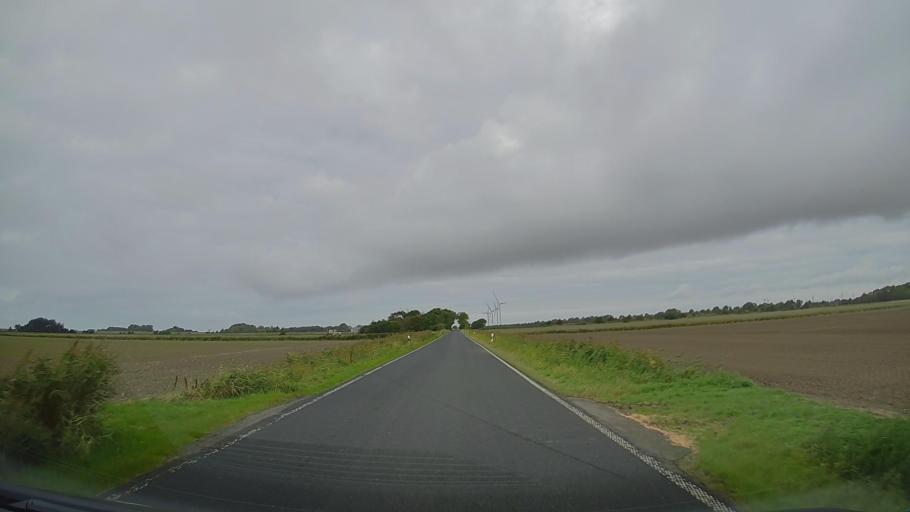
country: DE
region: Schleswig-Holstein
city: Galmsbull
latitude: 54.7581
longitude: 8.7247
